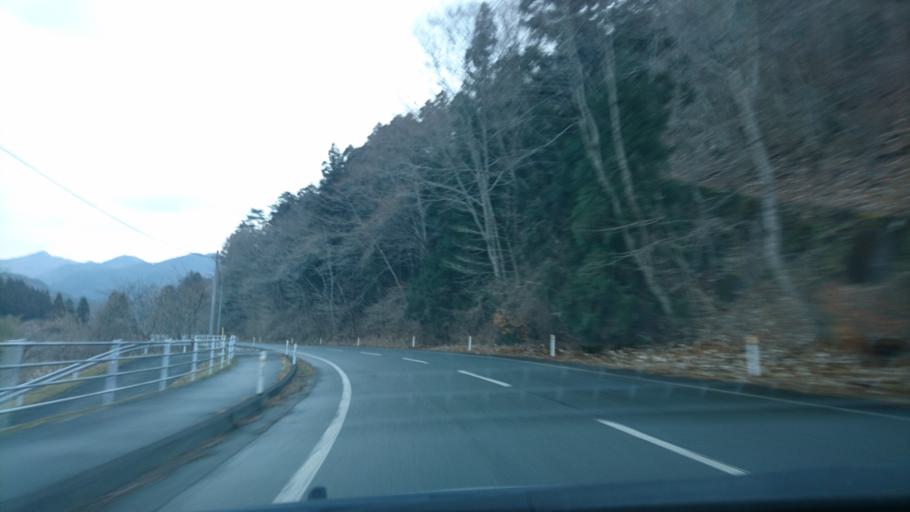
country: JP
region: Iwate
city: Ofunato
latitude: 39.0115
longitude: 141.5460
